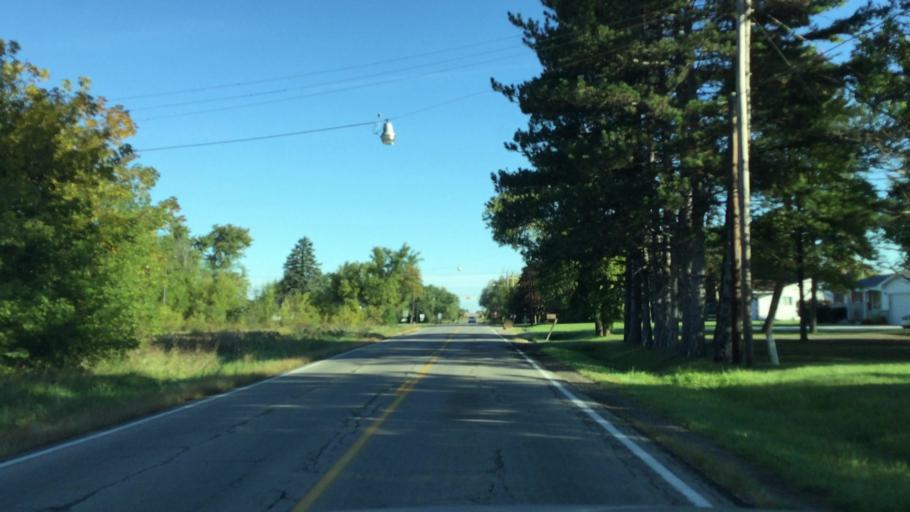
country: US
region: Michigan
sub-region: Genesee County
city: Beecher
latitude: 43.0883
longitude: -83.7536
